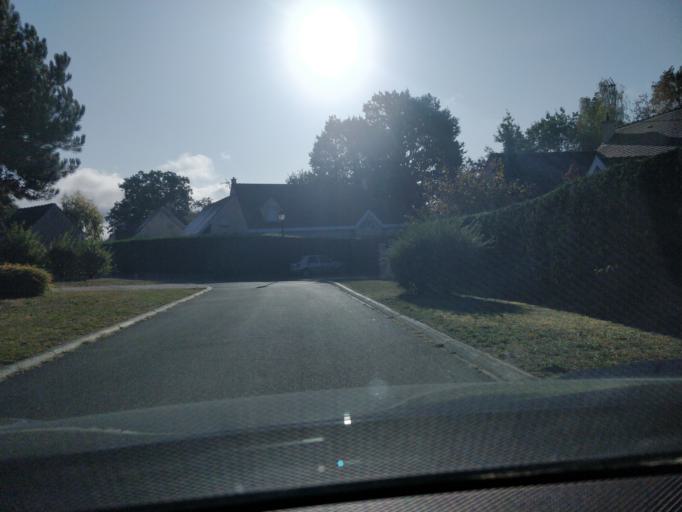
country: FR
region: Ile-de-France
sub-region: Departement de l'Essonne
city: Limours
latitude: 48.6300
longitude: 2.0764
